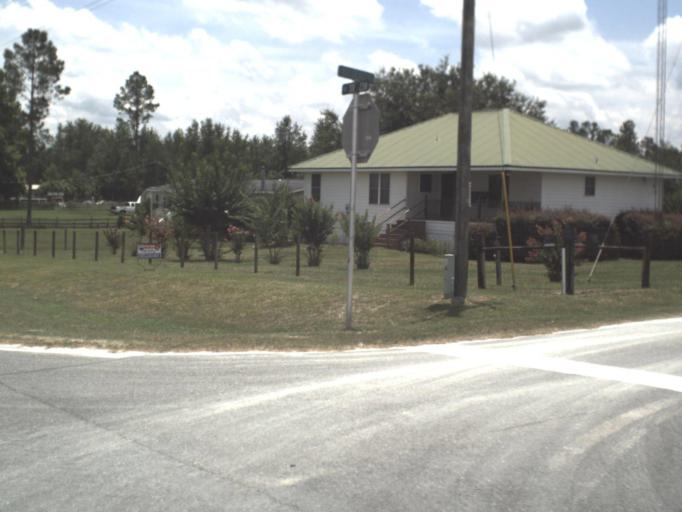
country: US
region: Florida
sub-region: Alachua County
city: High Springs
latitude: 30.0040
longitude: -82.5814
